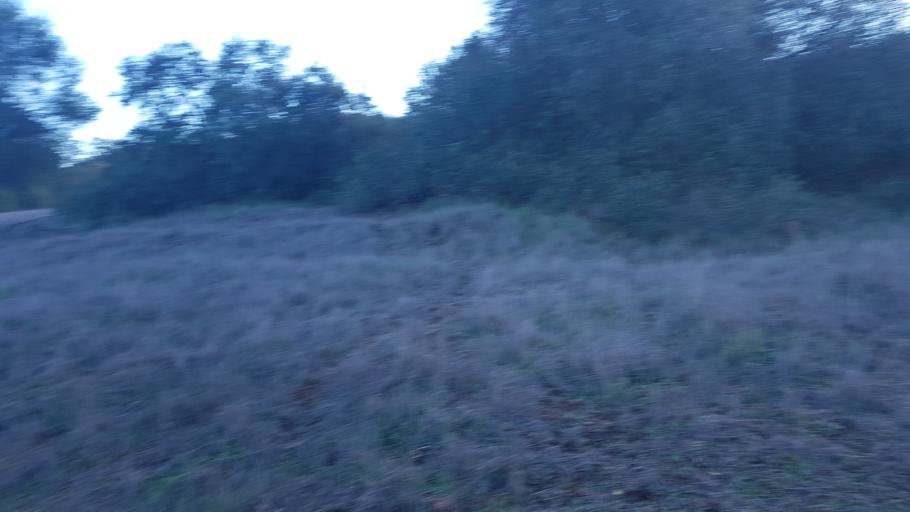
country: US
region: California
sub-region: San Diego County
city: Valley Center
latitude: 33.2062
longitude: -117.0629
